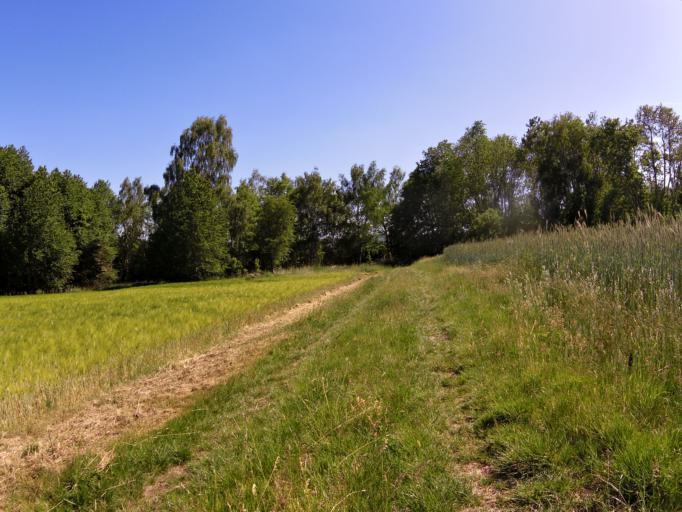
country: DE
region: Thuringia
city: Dippach
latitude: 50.9390
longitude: 10.0366
